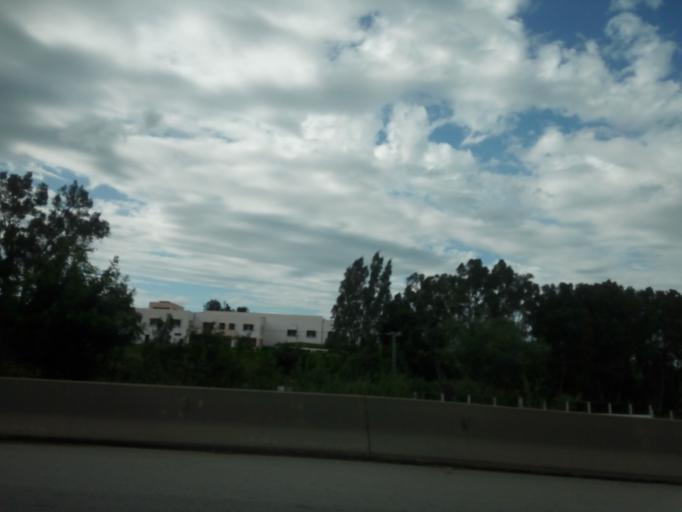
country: DZ
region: Tipaza
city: El Affroun
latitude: 36.4468
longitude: 2.6413
